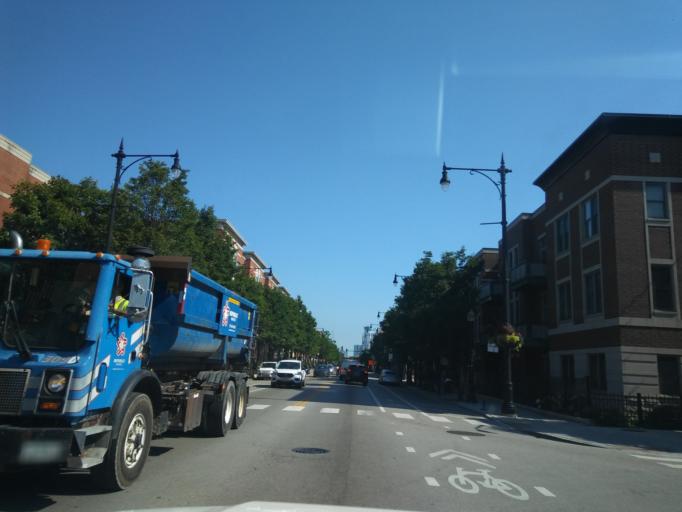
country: US
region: Illinois
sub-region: Cook County
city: Chicago
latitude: 41.8635
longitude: -87.6468
